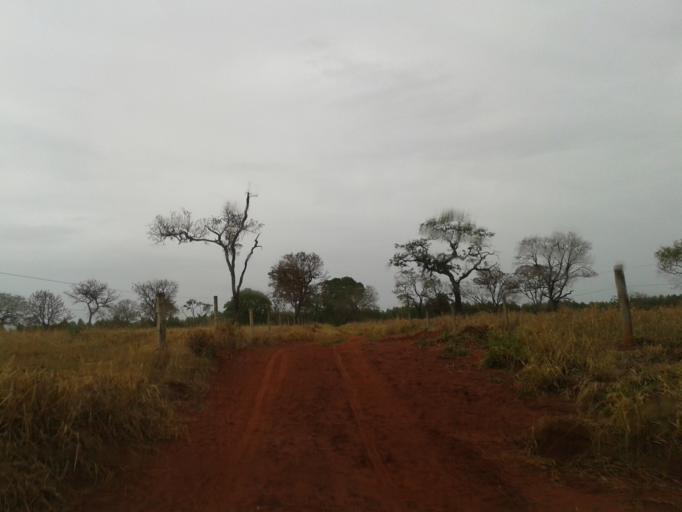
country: BR
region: Minas Gerais
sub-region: Campina Verde
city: Campina Verde
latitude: -19.3475
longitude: -49.5510
